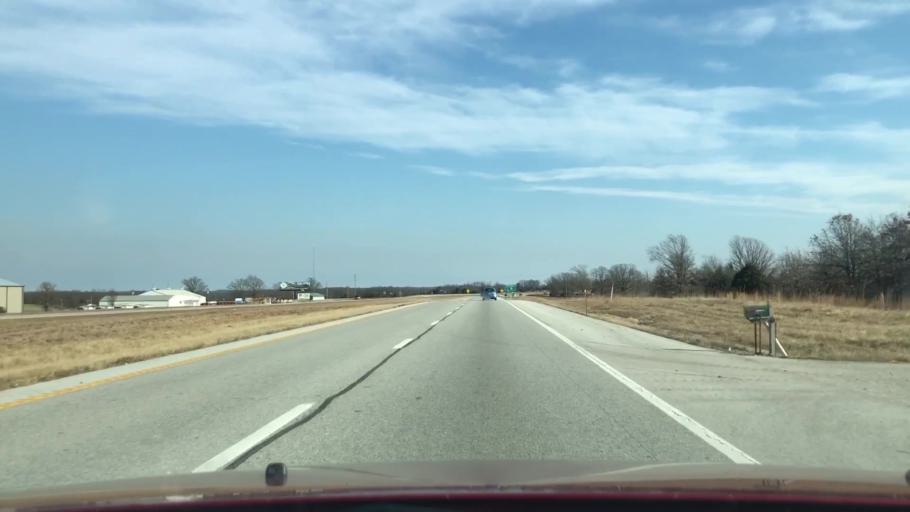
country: US
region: Missouri
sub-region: Webster County
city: Seymour
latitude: 37.1690
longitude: -92.8684
